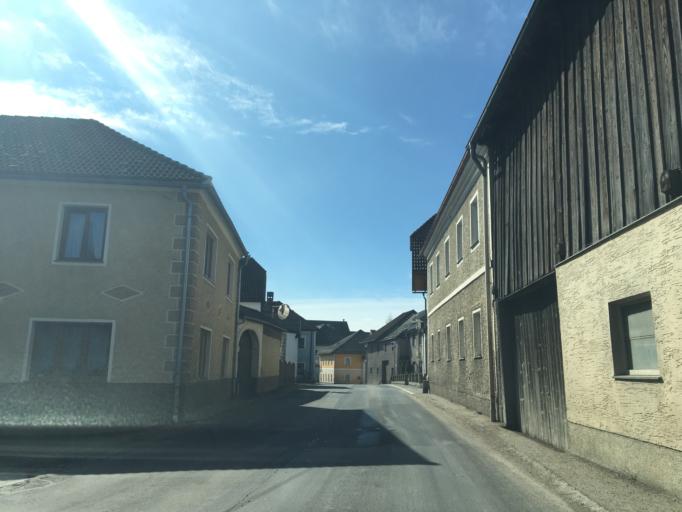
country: AT
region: Upper Austria
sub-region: Politischer Bezirk Perg
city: Sankt Georgen am Walde
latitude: 48.3667
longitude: 14.9098
